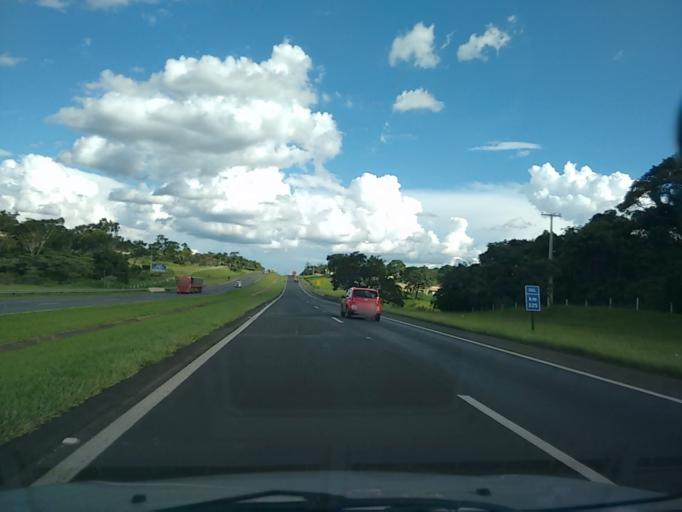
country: BR
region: Sao Paulo
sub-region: Sao Carlos
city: Sao Carlos
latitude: -22.0669
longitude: -47.8480
